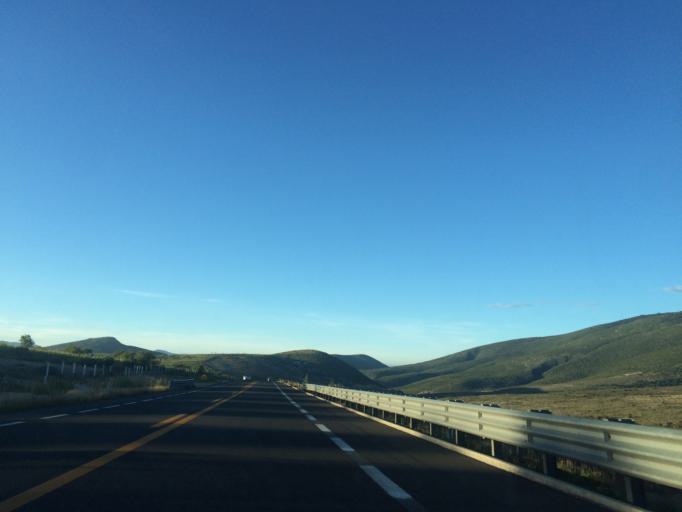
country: MX
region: Puebla
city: Morelos Canada
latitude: 18.6936
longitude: -97.4631
